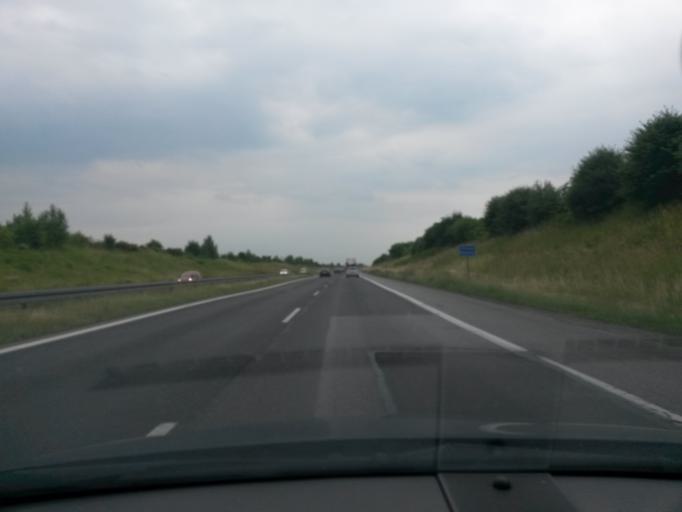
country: PL
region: Silesian Voivodeship
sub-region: Powiat czestochowski
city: Koscielec
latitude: 50.9010
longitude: 19.1975
